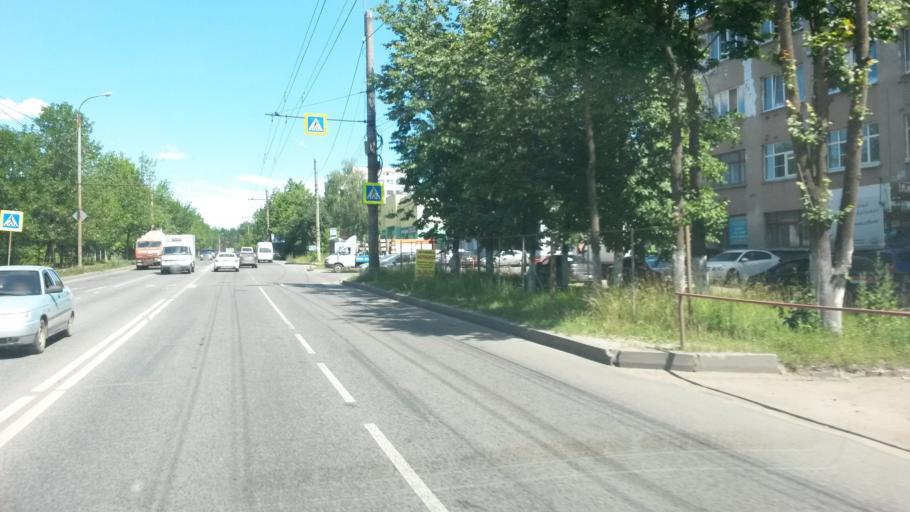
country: RU
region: Ivanovo
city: Kokhma
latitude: 56.9683
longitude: 41.0492
